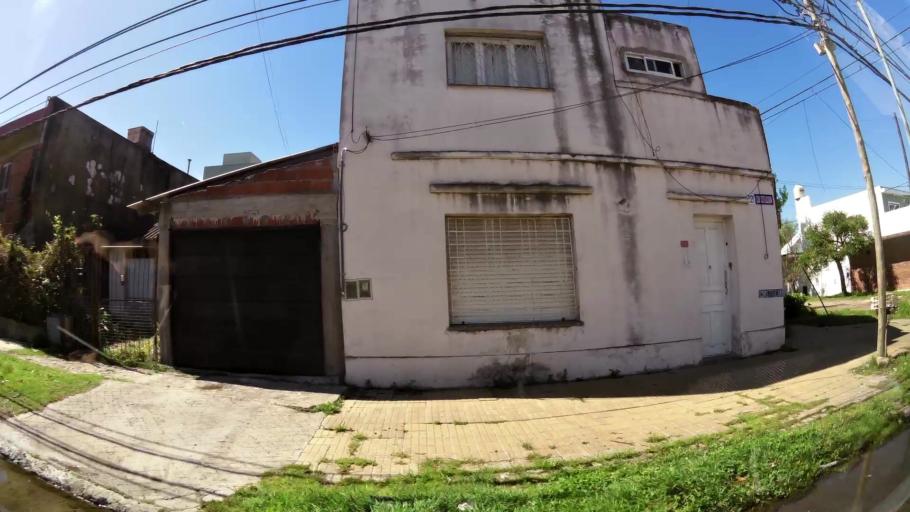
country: AR
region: Buenos Aires
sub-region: Partido de Quilmes
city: Quilmes
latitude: -34.6999
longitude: -58.2793
